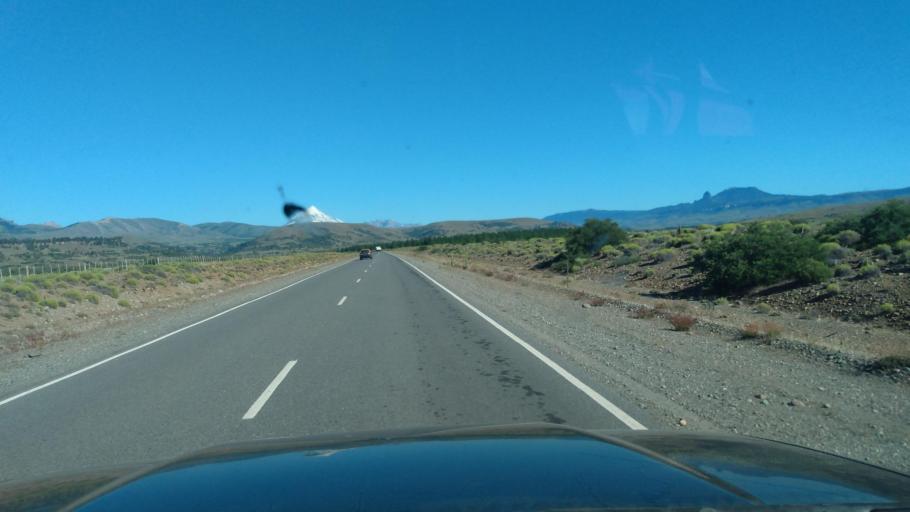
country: AR
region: Neuquen
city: Junin de los Andes
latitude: -39.8794
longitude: -71.1653
